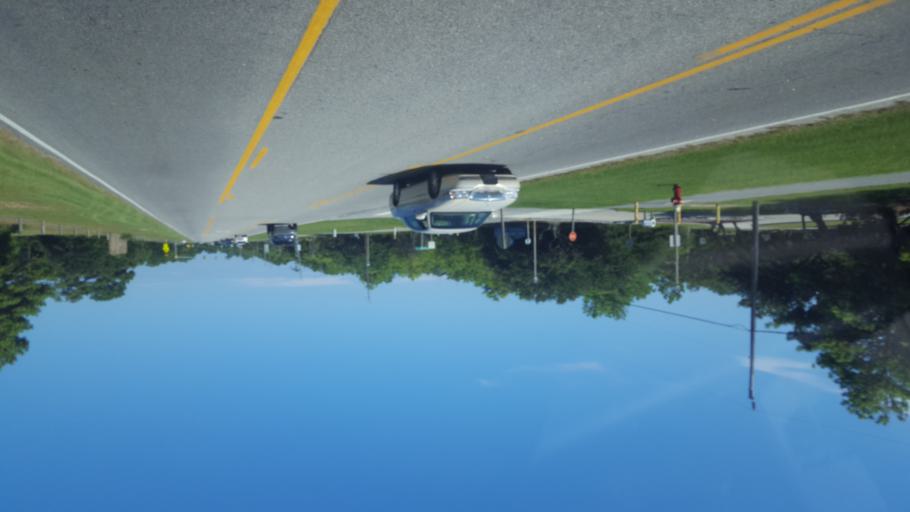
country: US
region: North Carolina
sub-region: Dare County
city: Kill Devil Hills
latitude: 36.0126
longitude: -75.6631
